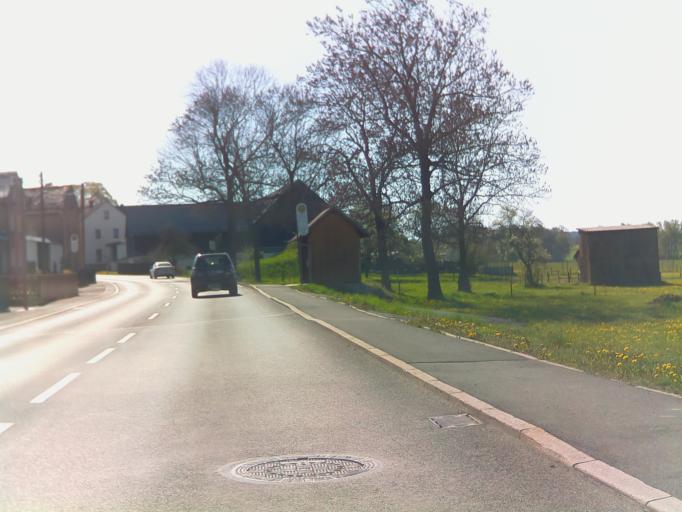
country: DE
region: Saxony
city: Mehltheuer
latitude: 50.5495
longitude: 12.0136
